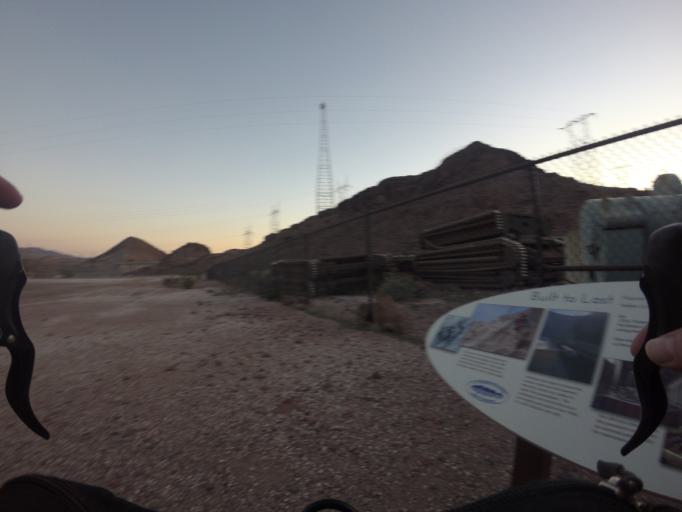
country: US
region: Nevada
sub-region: Clark County
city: Boulder City
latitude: 36.0200
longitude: -114.7473
